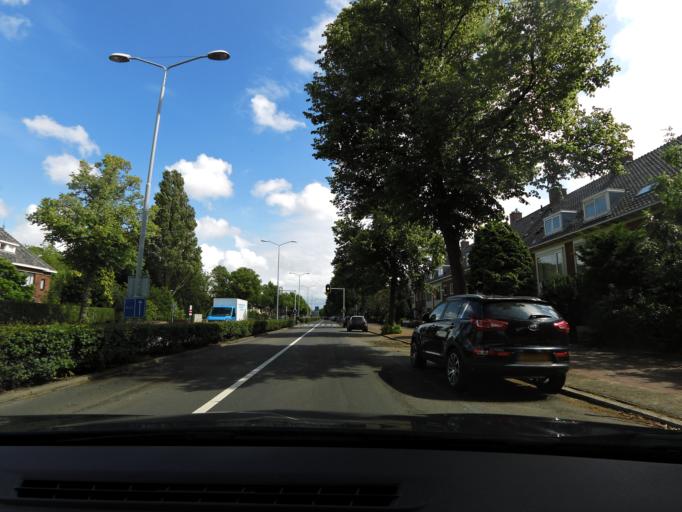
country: NL
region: South Holland
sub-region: Gemeente Leidschendam-Voorburg
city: Voorburg
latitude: 52.0724
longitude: 4.3522
